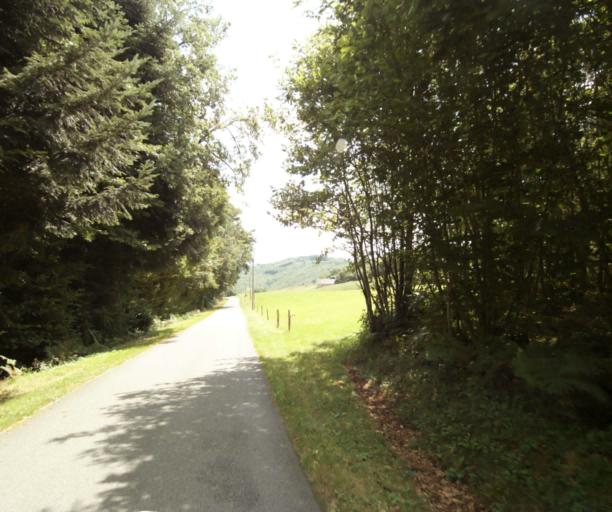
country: FR
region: Limousin
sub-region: Departement de la Correze
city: Sainte-Fortunade
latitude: 45.1759
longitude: 1.8304
